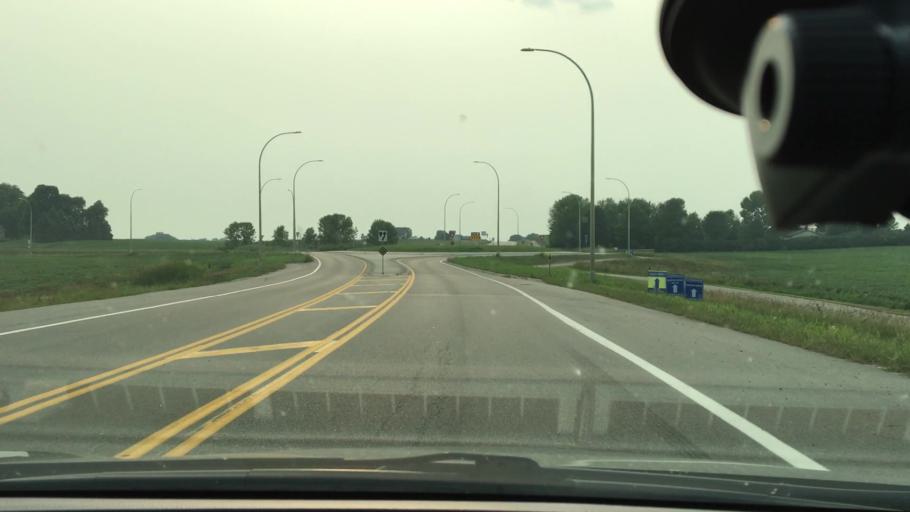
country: US
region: Minnesota
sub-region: Wright County
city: Otsego
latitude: 45.2524
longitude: -93.5988
